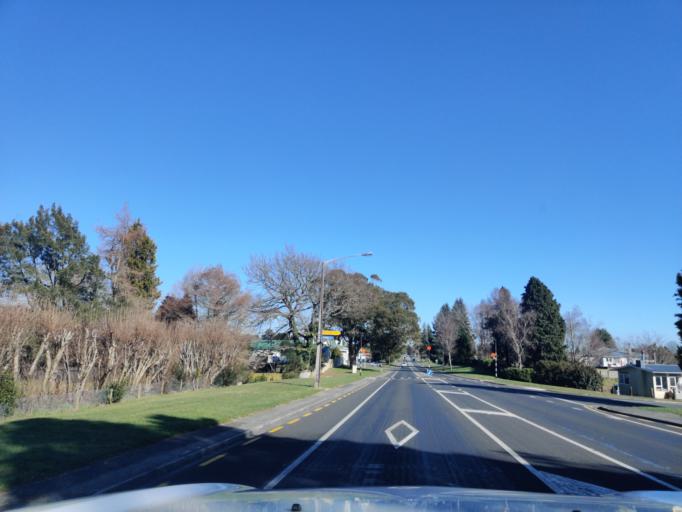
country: NZ
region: Waikato
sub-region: South Waikato District
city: Tokoroa
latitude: -38.2280
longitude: 175.8683
